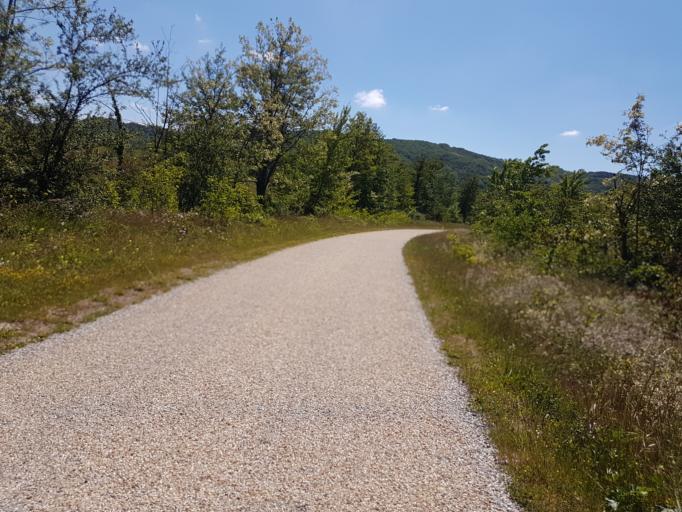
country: FR
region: Rhone-Alpes
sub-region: Departement de la Drome
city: Saint-Vallier
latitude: 45.1580
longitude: 4.8235
